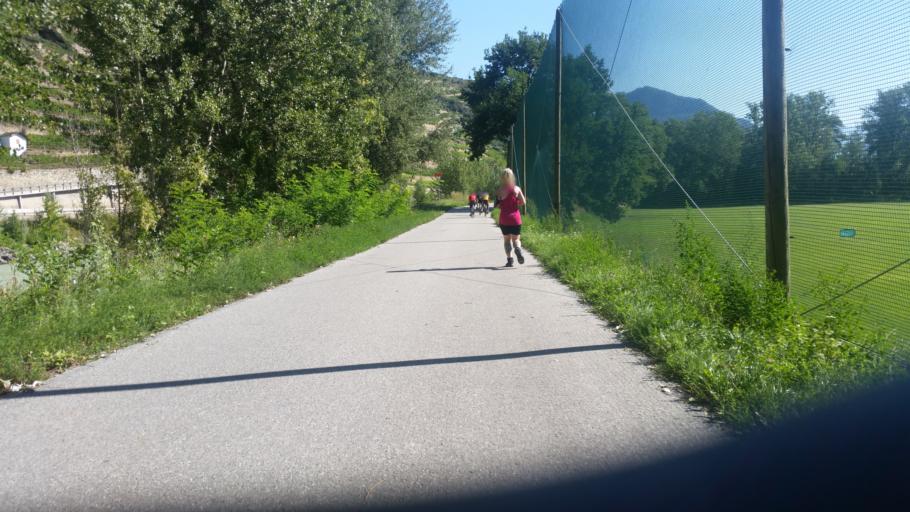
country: CH
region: Valais
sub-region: Sion District
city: Grimisuat
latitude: 46.2424
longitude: 7.3800
